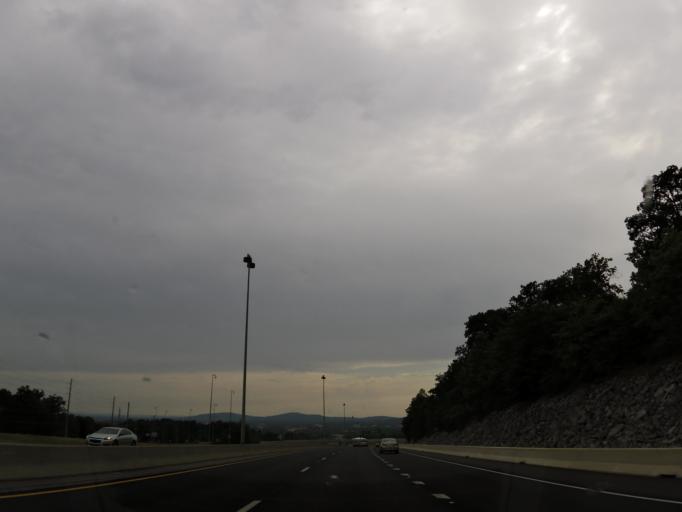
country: US
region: Alabama
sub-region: Madison County
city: Huntsville
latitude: 34.7629
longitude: -86.5589
